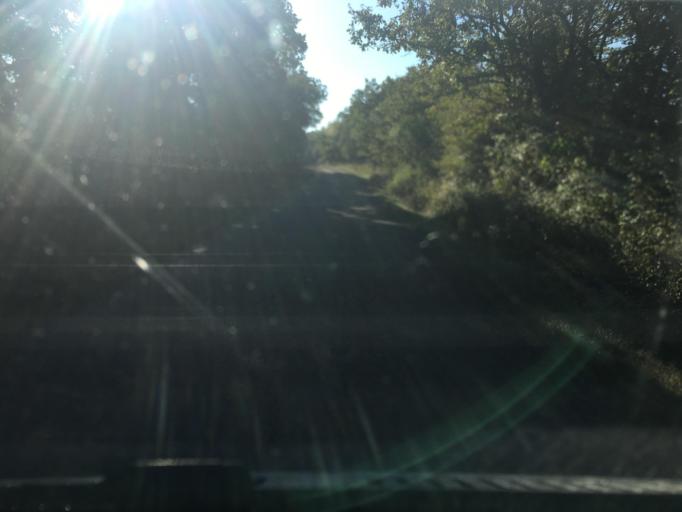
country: FR
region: Languedoc-Roussillon
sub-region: Departement du Gard
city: Goudargues
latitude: 44.1742
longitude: 4.3426
